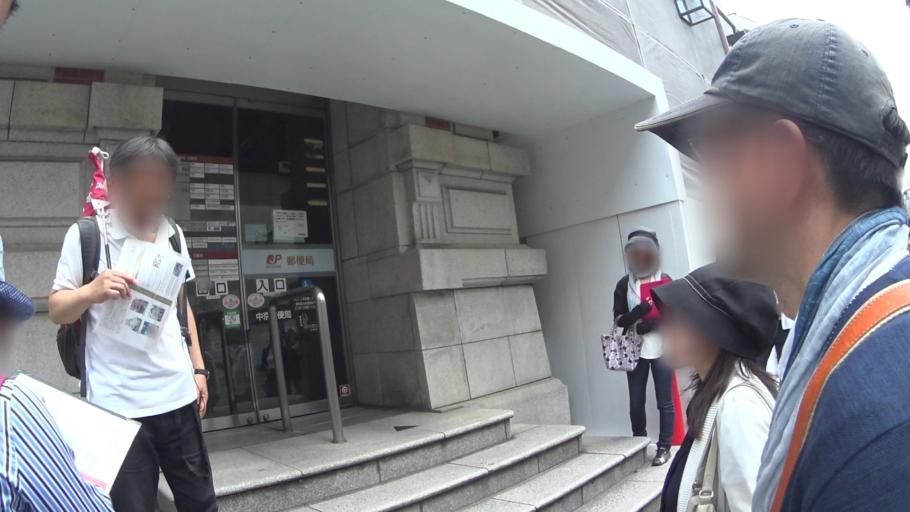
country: JP
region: Kyoto
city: Kyoto
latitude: 35.0087
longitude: 135.7614
